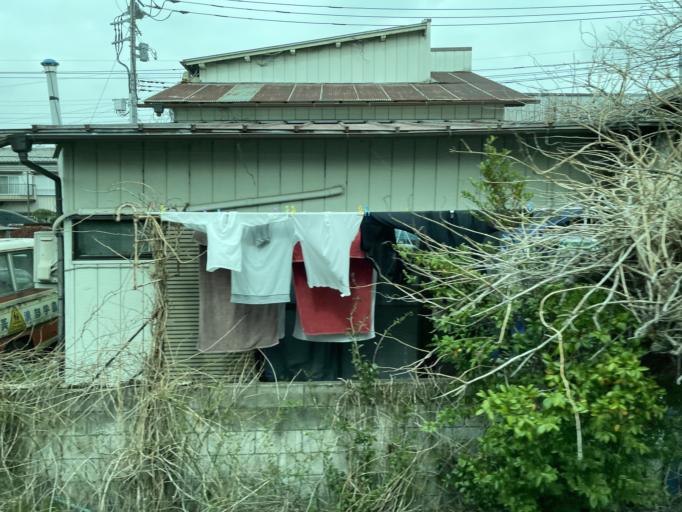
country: JP
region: Saitama
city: Kukichuo
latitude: 36.0567
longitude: 139.6787
